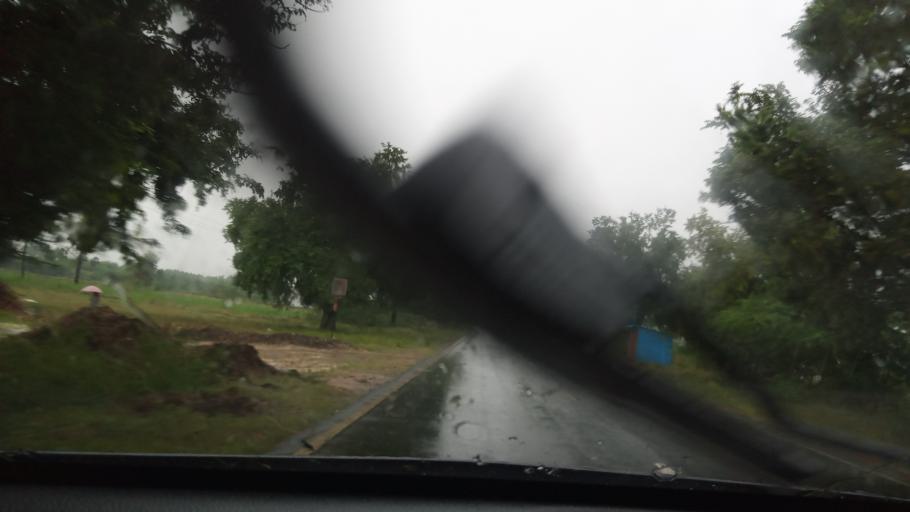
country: IN
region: Tamil Nadu
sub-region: Vellore
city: Kalavai
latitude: 12.8417
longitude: 79.4014
